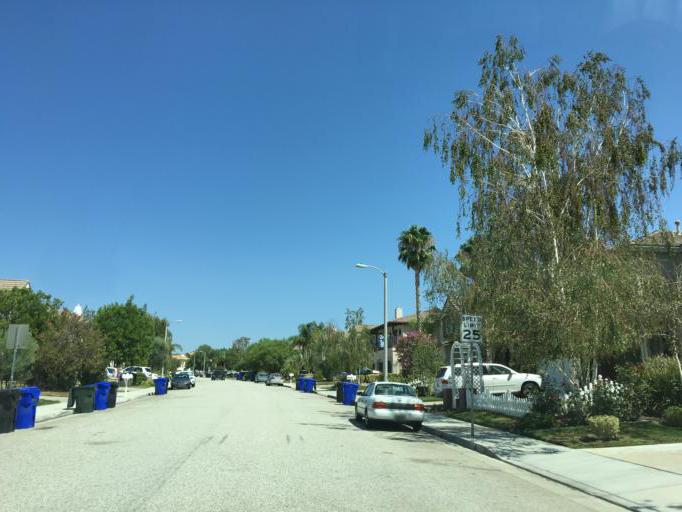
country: US
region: California
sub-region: Los Angeles County
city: Santa Clarita
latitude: 34.3858
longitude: -118.5999
